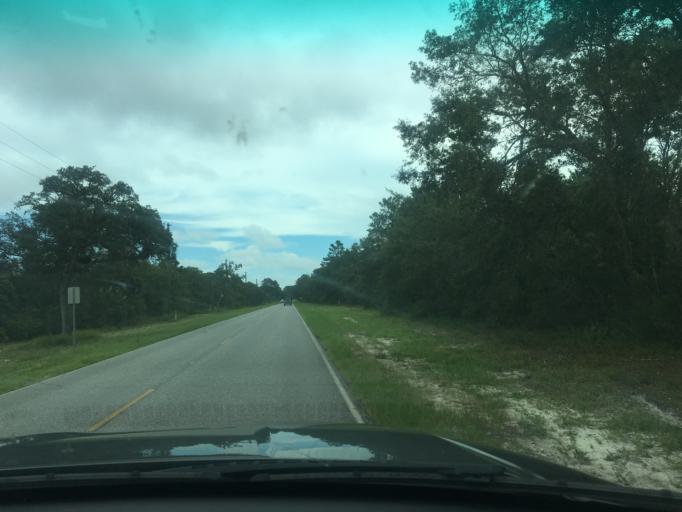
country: US
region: Florida
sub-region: Wakulla County
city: Crawfordville
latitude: 29.9061
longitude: -84.3554
